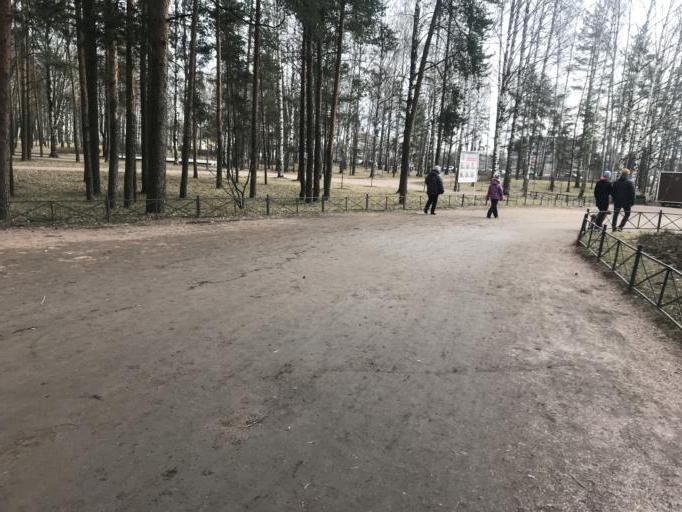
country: RU
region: St.-Petersburg
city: Sosnovka
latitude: 60.0144
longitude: 30.3520
